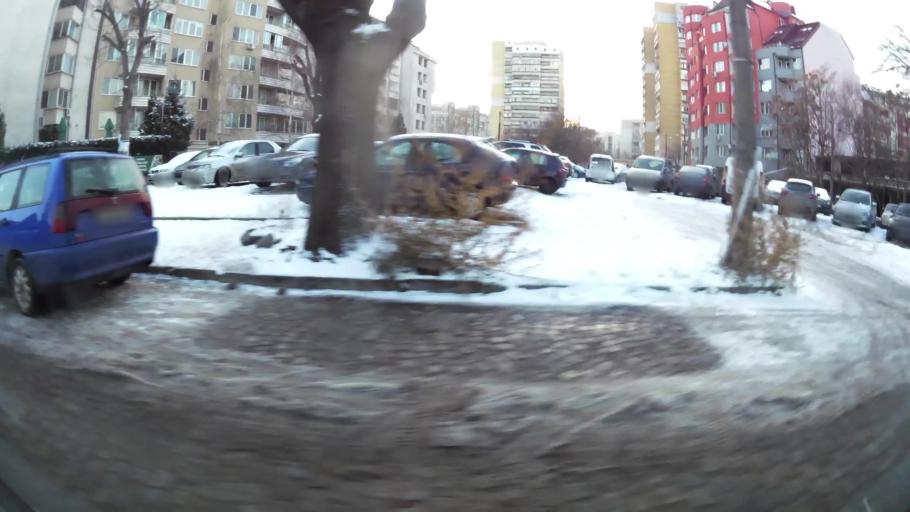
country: BG
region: Sofia-Capital
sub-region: Stolichna Obshtina
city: Sofia
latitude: 42.6816
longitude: 23.3733
